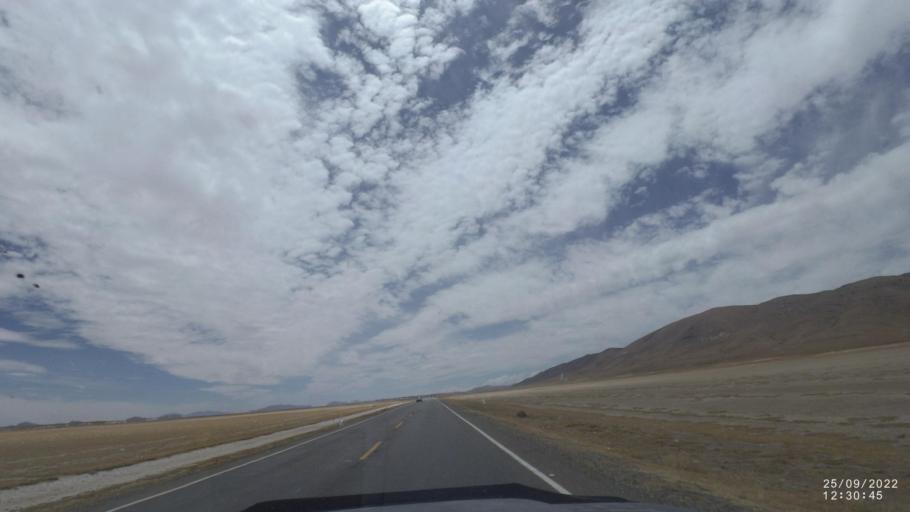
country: BO
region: Oruro
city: Machacamarca
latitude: -18.2453
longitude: -67.0026
